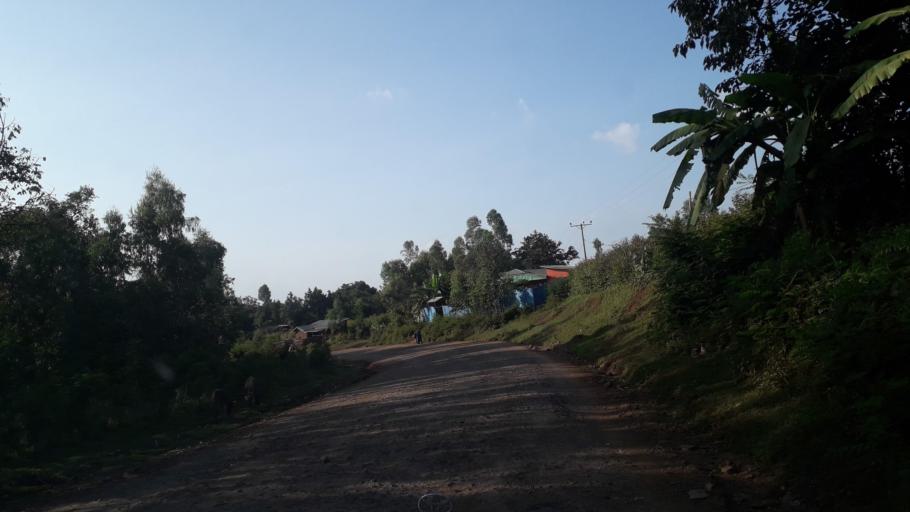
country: ET
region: Oromiya
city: Jima
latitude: 7.5448
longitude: 36.8754
